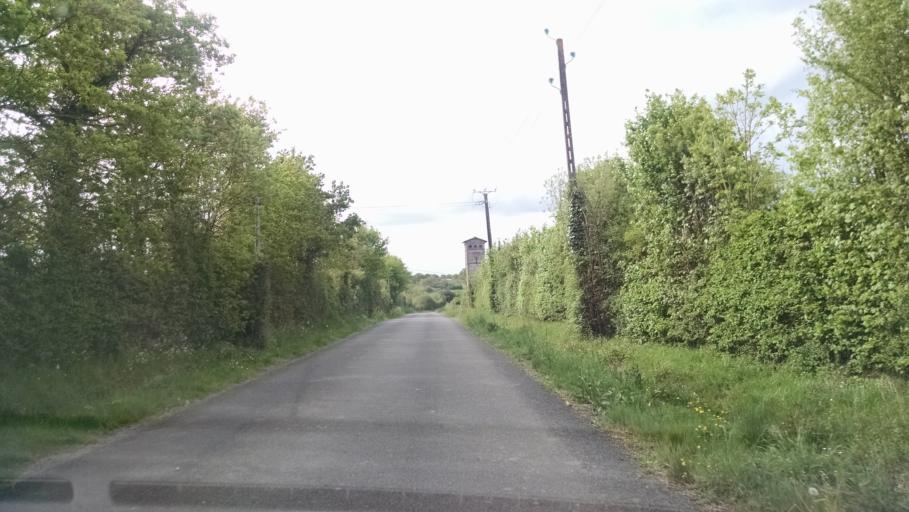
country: FR
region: Pays de la Loire
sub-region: Departement de la Vendee
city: Saint-Hilaire-de-Loulay
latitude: 46.9894
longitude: -1.3482
